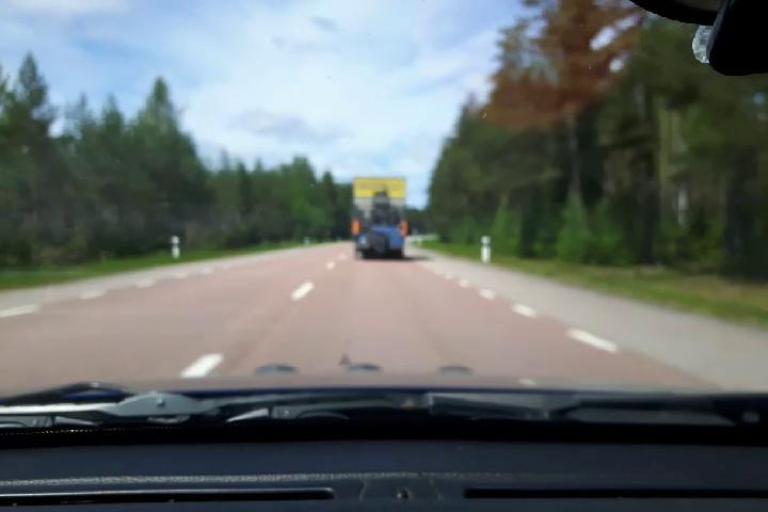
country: SE
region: Uppsala
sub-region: Tierps Kommun
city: Tierp
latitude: 60.1804
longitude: 17.4802
